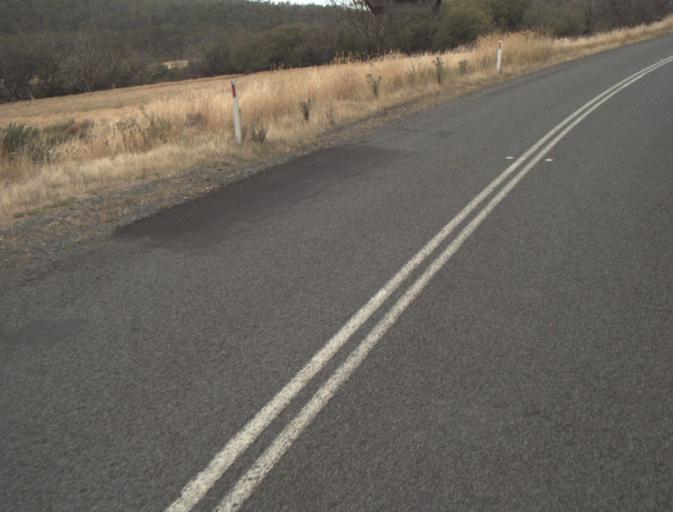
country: AU
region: Tasmania
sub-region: Northern Midlands
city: Evandale
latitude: -41.4971
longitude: 147.4065
